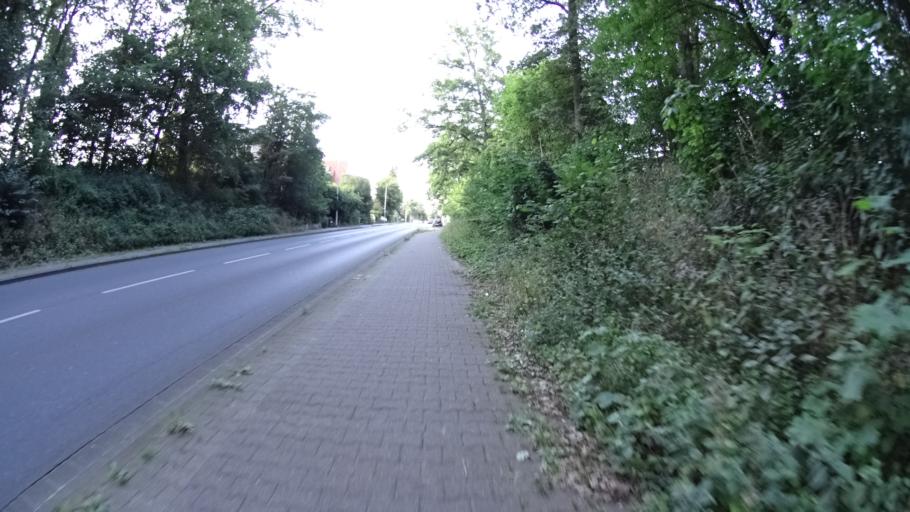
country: DE
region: Lower Saxony
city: Lueneburg
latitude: 53.2286
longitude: 10.3946
